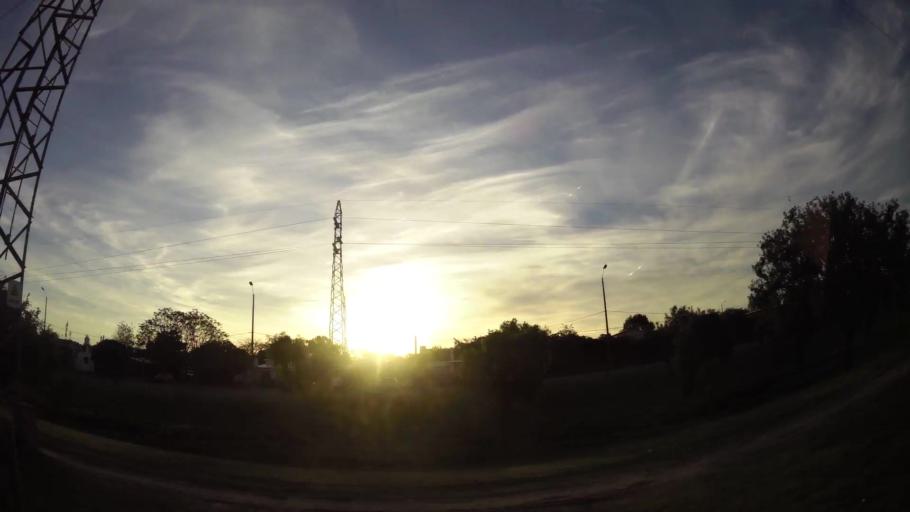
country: UY
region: Maldonado
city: Maldonado
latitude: -34.9088
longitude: -54.9465
